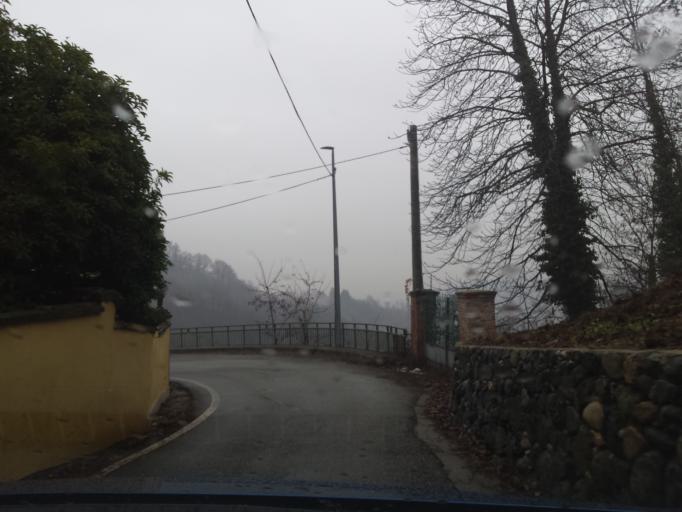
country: IT
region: Piedmont
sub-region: Provincia di Torino
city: Revigliasco
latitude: 45.0532
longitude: 7.7331
